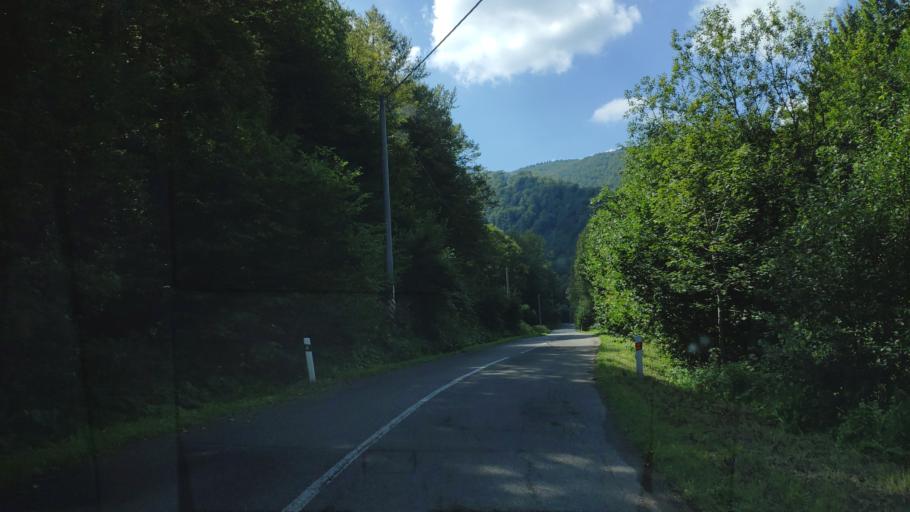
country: PL
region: Subcarpathian Voivodeship
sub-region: Powiat leski
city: Cisna
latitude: 49.0720
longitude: 22.3715
